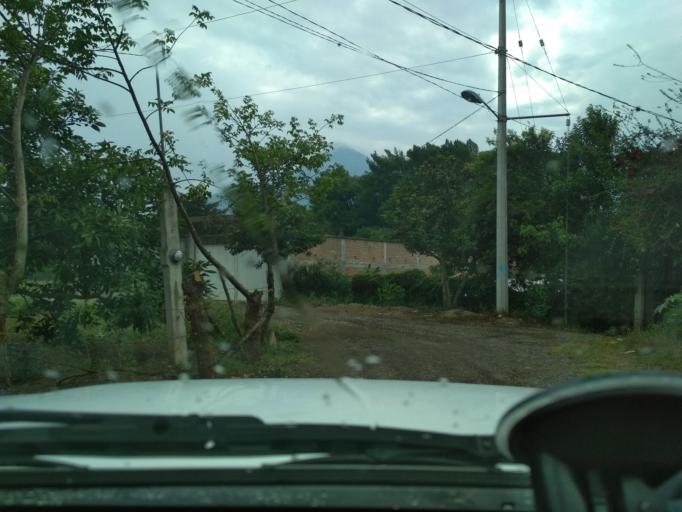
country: MX
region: Veracruz
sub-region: Nogales
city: Taza de Agua Ojo Zarco
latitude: 18.7788
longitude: -97.2049
